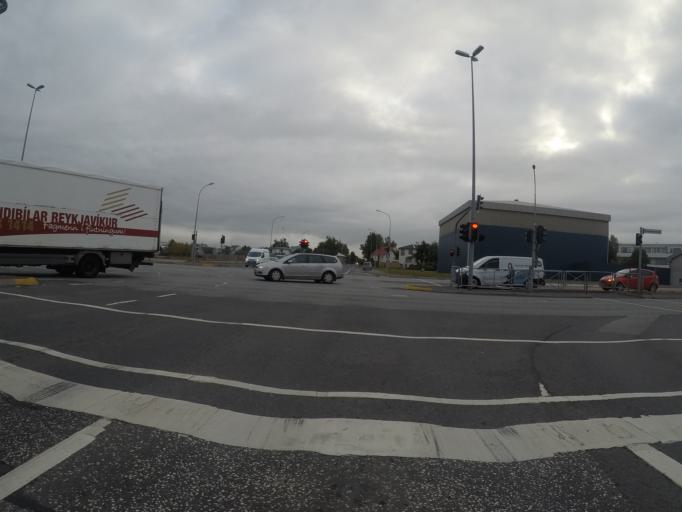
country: IS
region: Capital Region
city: Reykjavik
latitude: 64.1462
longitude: -21.8932
